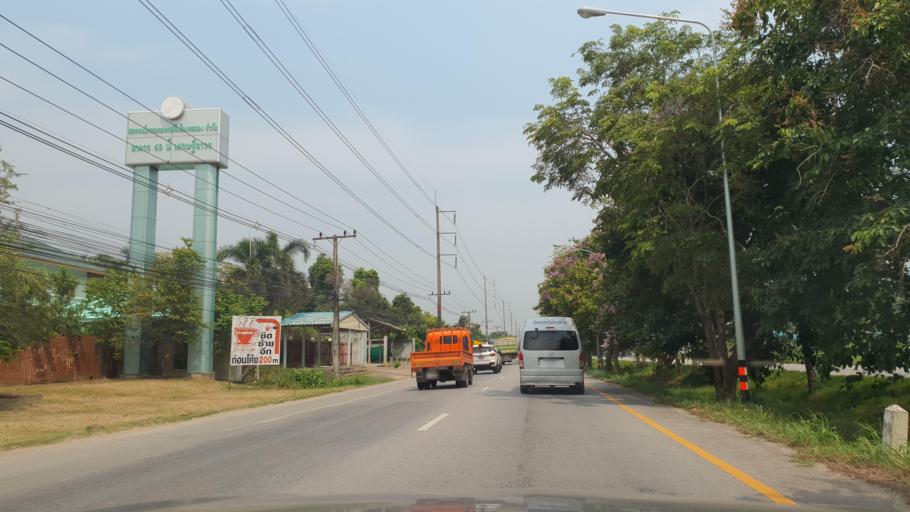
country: TH
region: Rayong
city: Rayong
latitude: 12.6419
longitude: 101.3583
